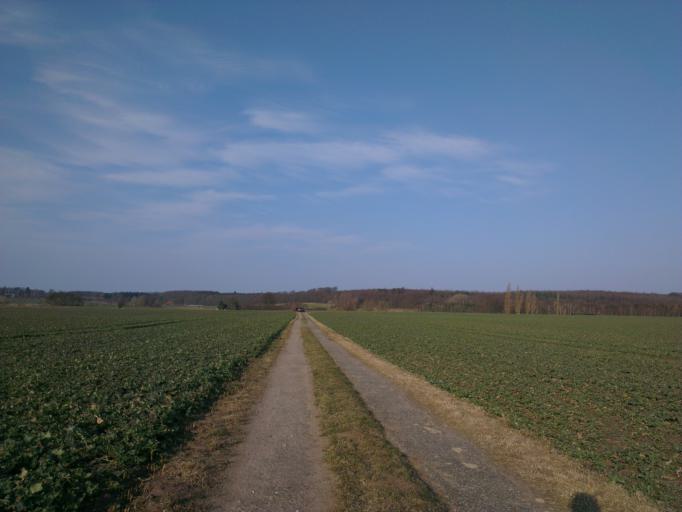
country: DK
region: Capital Region
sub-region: Frederikssund Kommune
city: Jaegerspris
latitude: 55.8368
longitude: 12.0073
